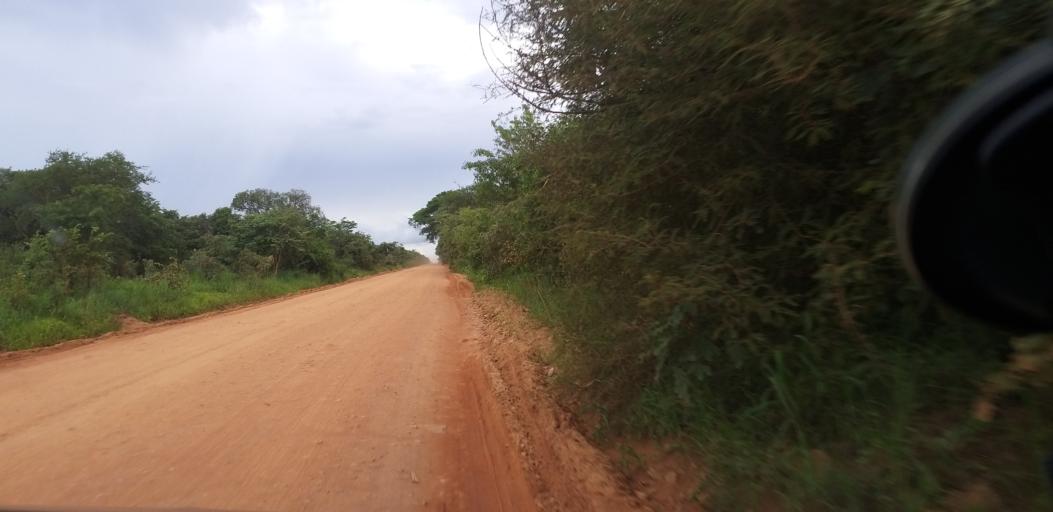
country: ZM
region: Lusaka
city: Lusaka
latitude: -15.2024
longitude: 28.4386
